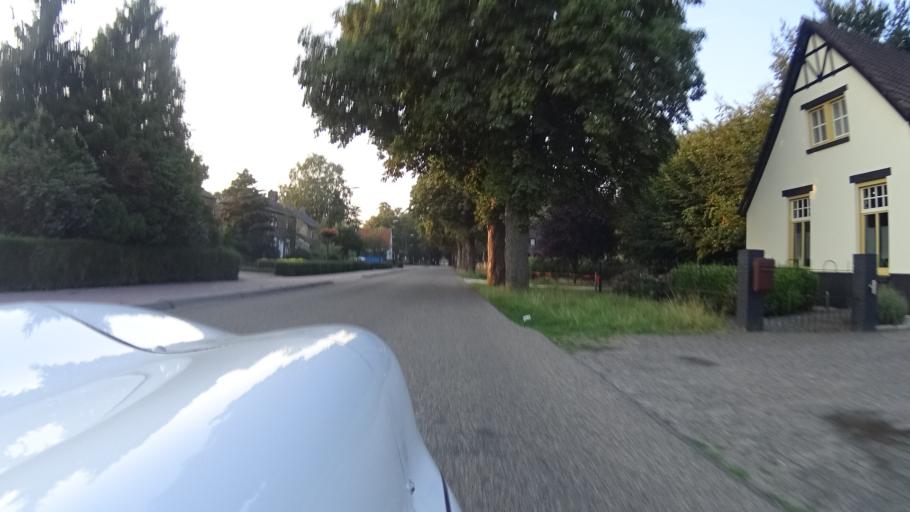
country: NL
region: North Brabant
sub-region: Gemeente Sint Anthonis
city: Sint Anthonis
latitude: 51.6046
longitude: 5.9140
